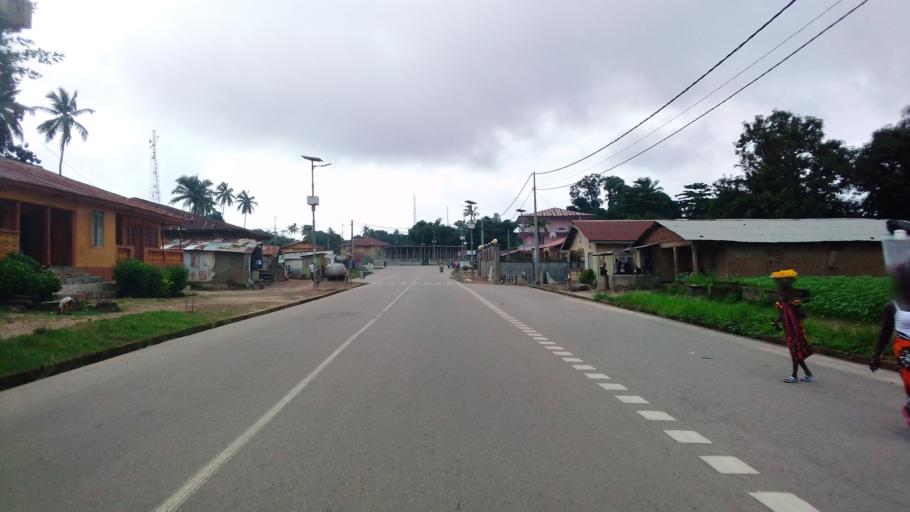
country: SL
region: Northern Province
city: Lunsar
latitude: 8.6862
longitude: -12.5360
